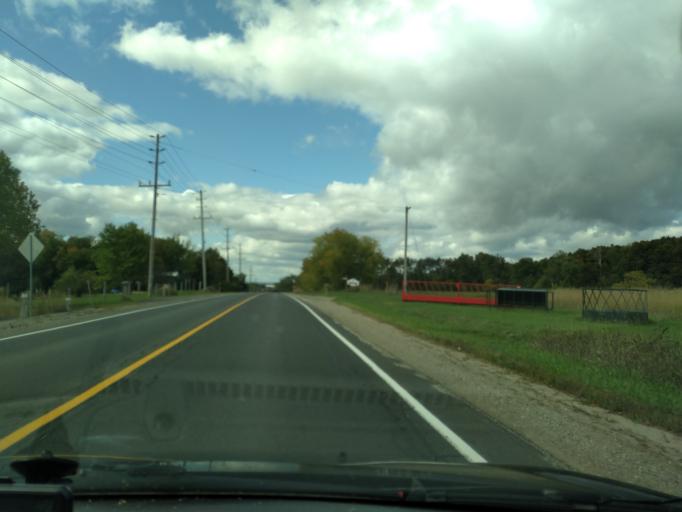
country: CA
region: Ontario
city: Angus
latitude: 44.2587
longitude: -79.7795
